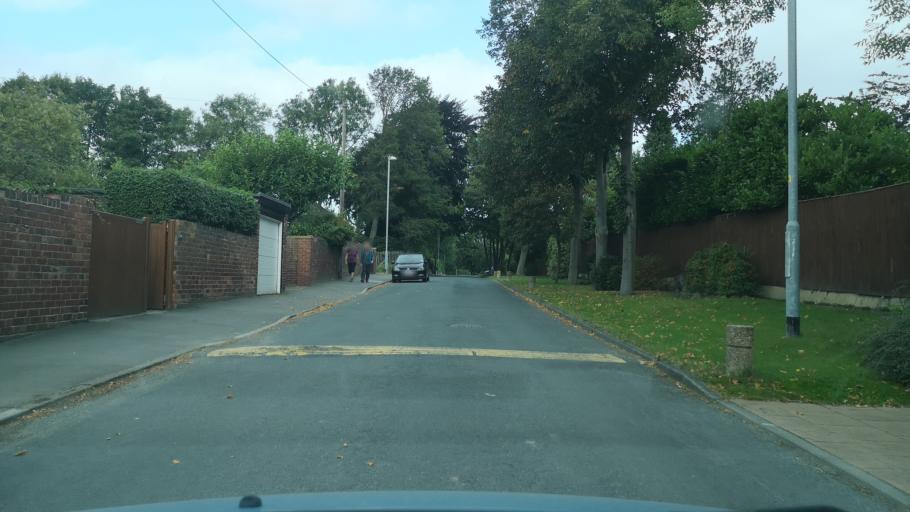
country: GB
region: England
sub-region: City and Borough of Wakefield
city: Walton
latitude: 53.6566
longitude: -1.4883
